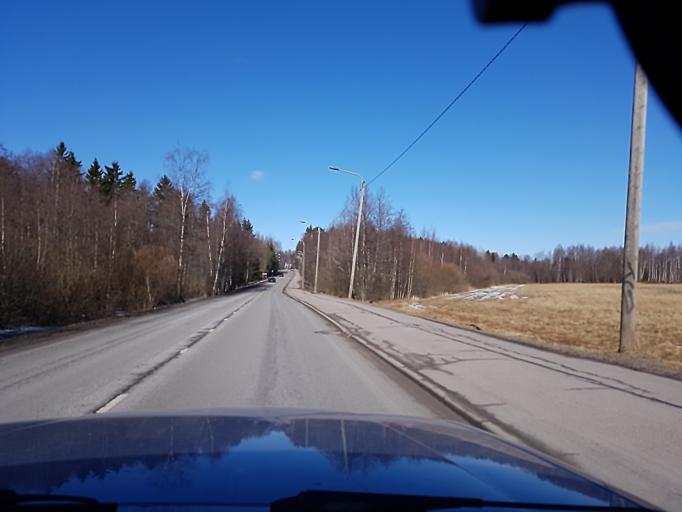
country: FI
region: Uusimaa
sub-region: Helsinki
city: Teekkarikylae
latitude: 60.2665
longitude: 24.8634
